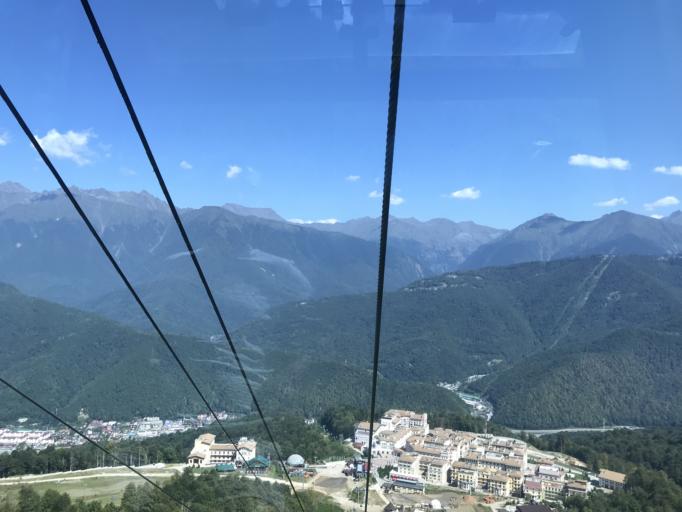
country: RU
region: Krasnodarskiy
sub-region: Sochi City
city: Krasnaya Polyana
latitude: 43.6637
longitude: 40.2547
